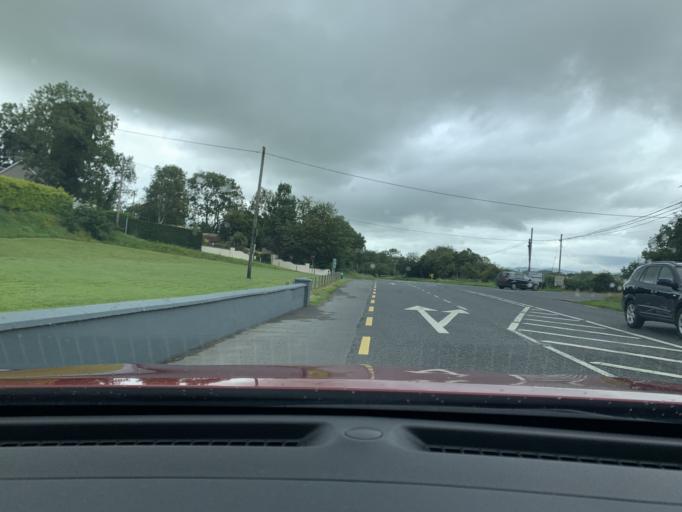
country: IE
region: Ulster
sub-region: County Donegal
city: Leifear
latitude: 54.7936
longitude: -7.5516
